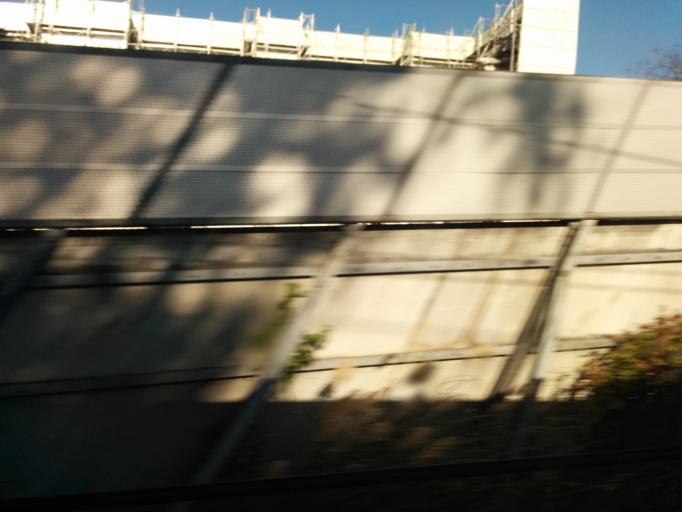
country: JP
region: Kanagawa
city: Yokohama
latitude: 35.4703
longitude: 139.5514
